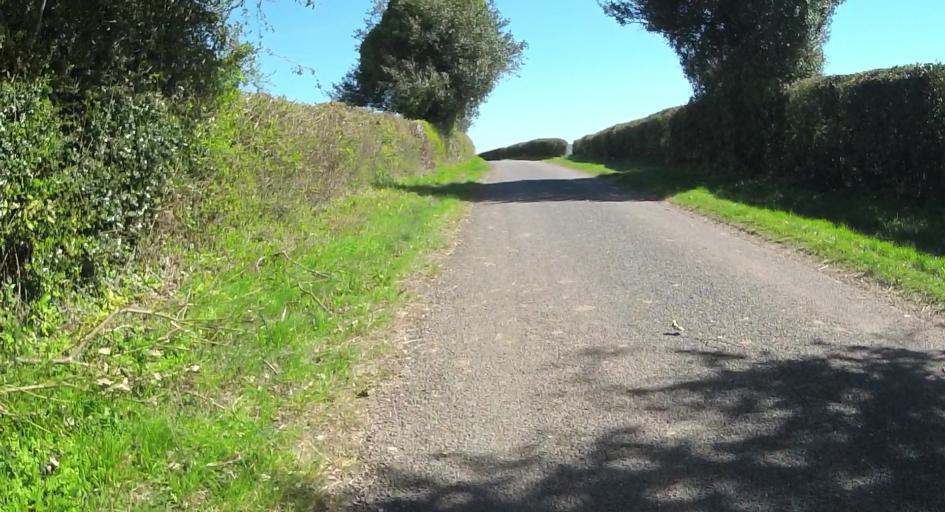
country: GB
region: England
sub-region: Hampshire
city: Old Basing
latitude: 51.2463
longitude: -1.0369
